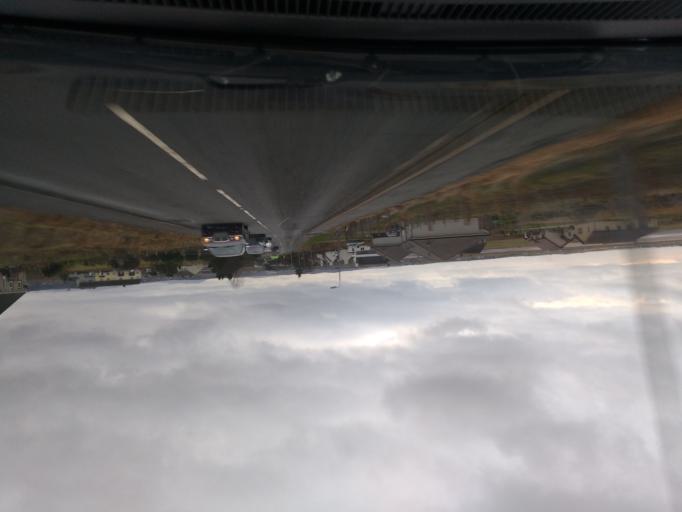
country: GB
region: Scotland
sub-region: Eilean Siar
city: Isle of Lewis
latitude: 58.2432
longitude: -6.3499
